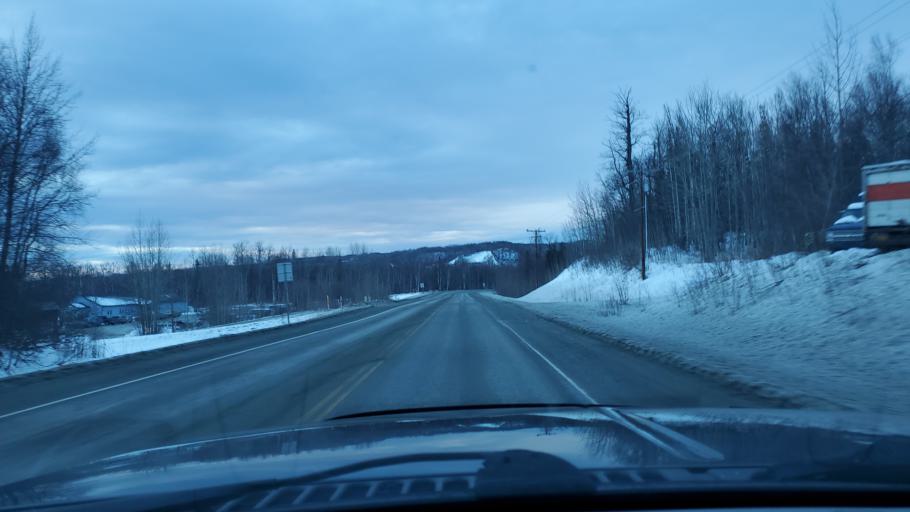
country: US
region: Alaska
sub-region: Matanuska-Susitna Borough
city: Lazy Mountain
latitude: 61.6776
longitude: -149.0175
